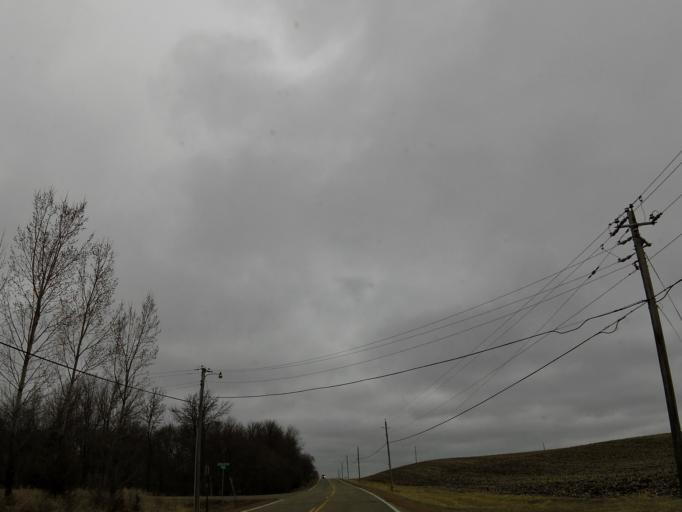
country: US
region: Minnesota
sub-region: Scott County
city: Shakopee
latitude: 44.7406
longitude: -93.5420
